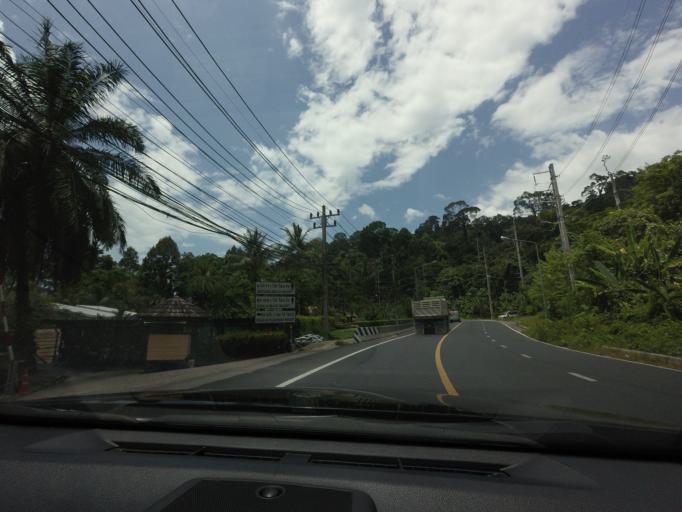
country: TH
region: Phangnga
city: Ban Khao Lak
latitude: 8.6305
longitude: 98.2461
